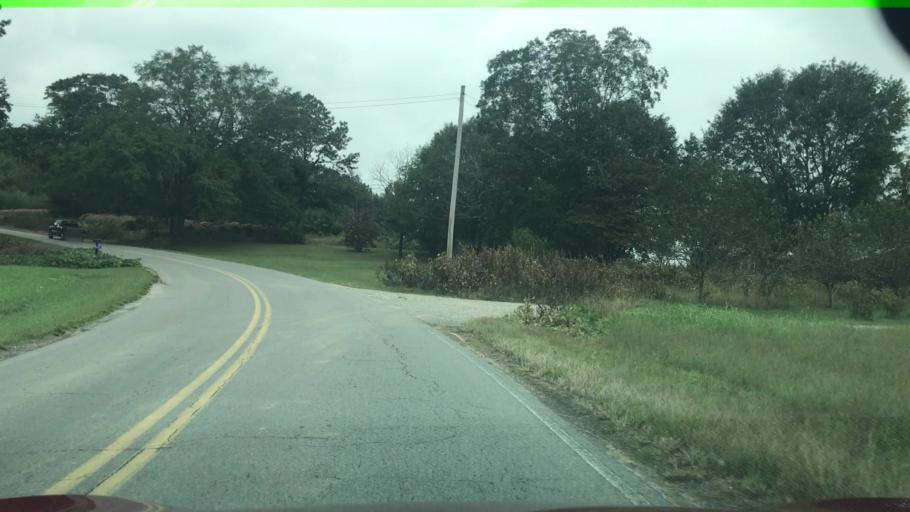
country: US
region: Alabama
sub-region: Cullman County
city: Good Hope
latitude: 34.0970
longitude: -87.0489
